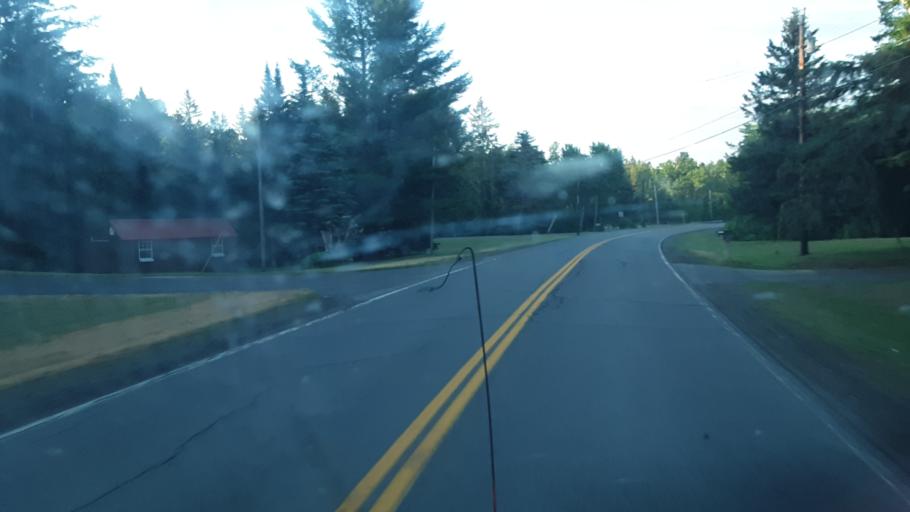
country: US
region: Maine
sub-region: Aroostook County
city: Presque Isle
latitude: 46.7311
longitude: -68.0293
